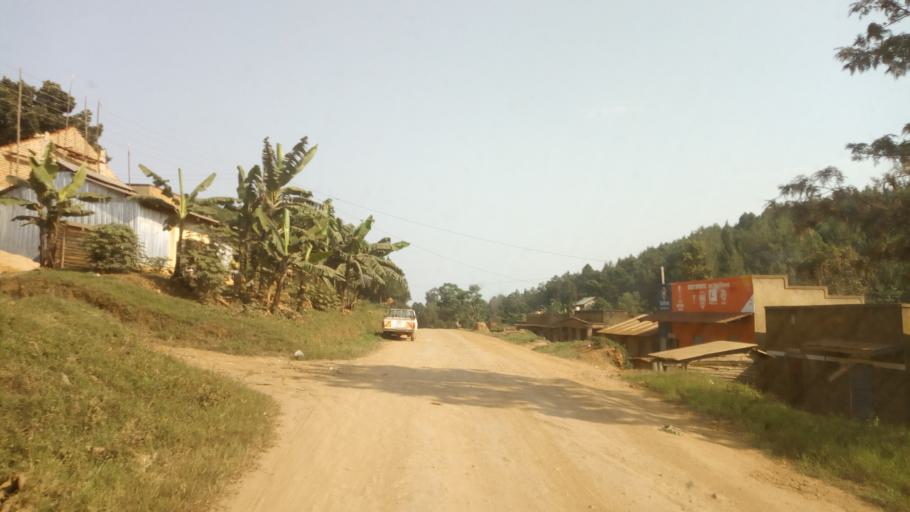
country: UG
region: Western Region
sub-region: Kanungu District
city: Ntungamo
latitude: -0.8290
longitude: 29.7088
